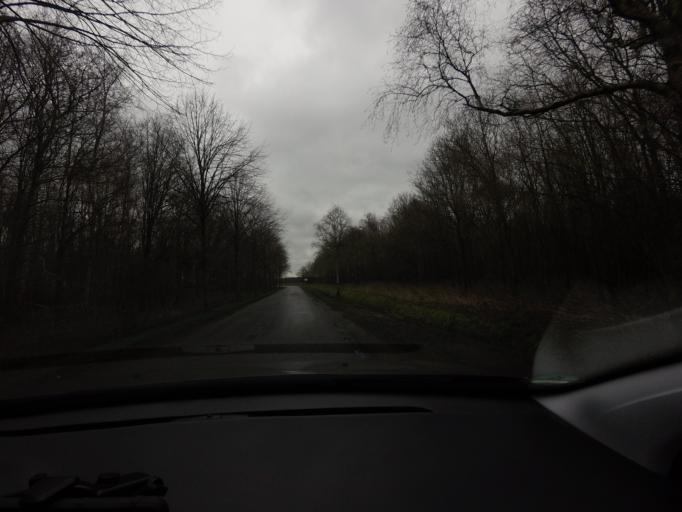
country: NL
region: Drenthe
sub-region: Gemeente Hoogeveen
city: Hoogeveen
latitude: 52.7738
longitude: 6.4970
